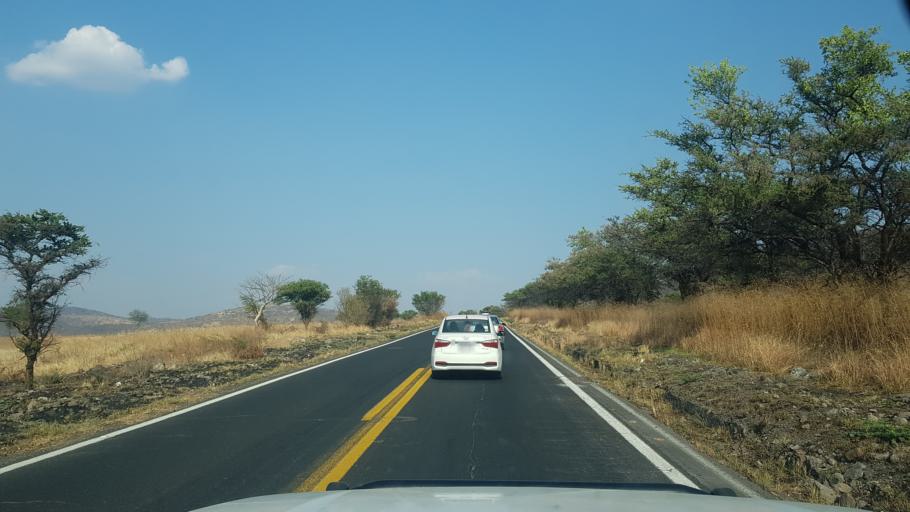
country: MX
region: Puebla
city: Calmeca
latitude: 18.6547
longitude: -98.6563
